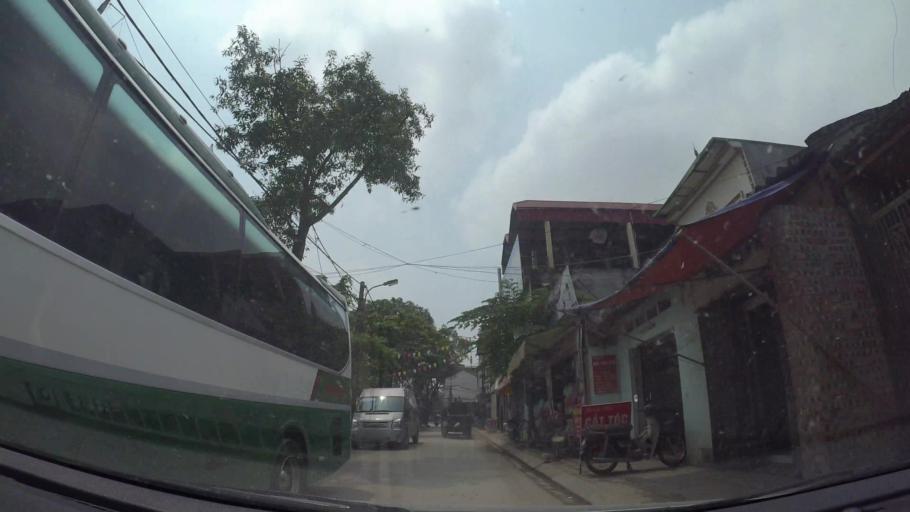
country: VN
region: Ha Noi
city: Tay Ho
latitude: 21.0873
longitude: 105.7880
